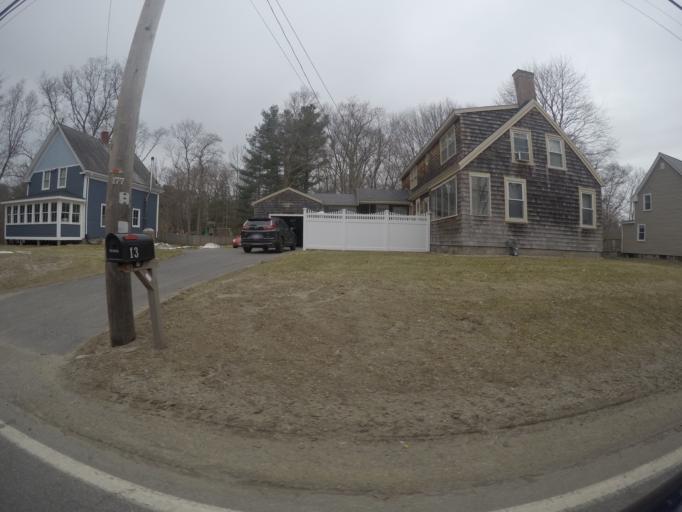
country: US
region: Massachusetts
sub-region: Bristol County
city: Easton
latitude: 42.0420
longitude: -71.0679
